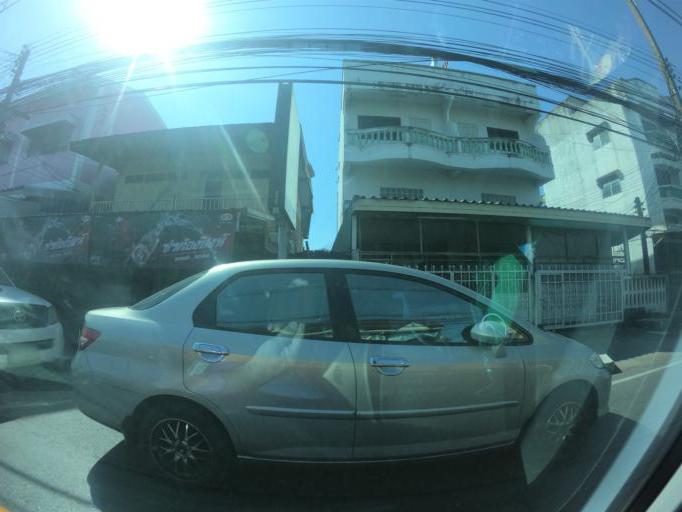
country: TH
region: Khon Kaen
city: Khon Kaen
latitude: 16.4126
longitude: 102.8338
